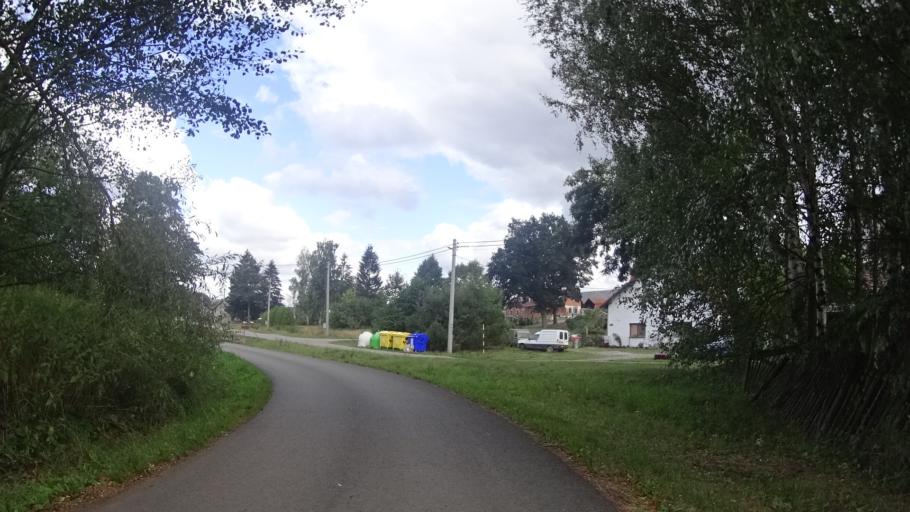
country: CZ
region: Pardubicky
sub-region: Okres Usti nad Orlici
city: Lanskroun
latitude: 49.9206
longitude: 16.5581
